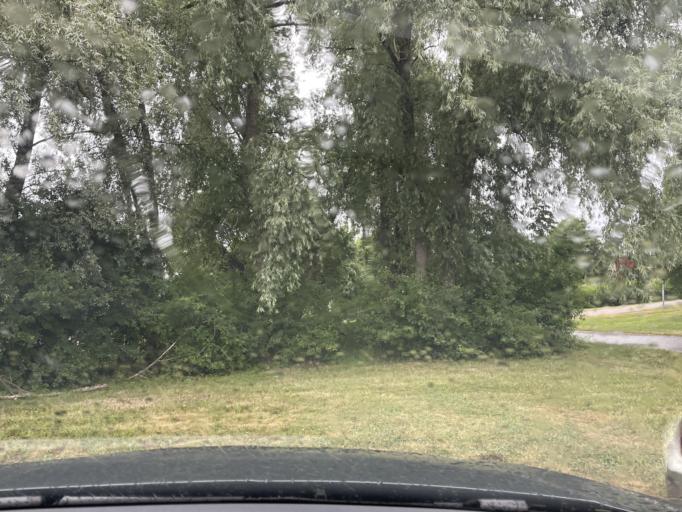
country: SE
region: Stockholm
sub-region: Jarfalla Kommun
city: Jakobsberg
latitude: 59.4215
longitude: 17.8273
